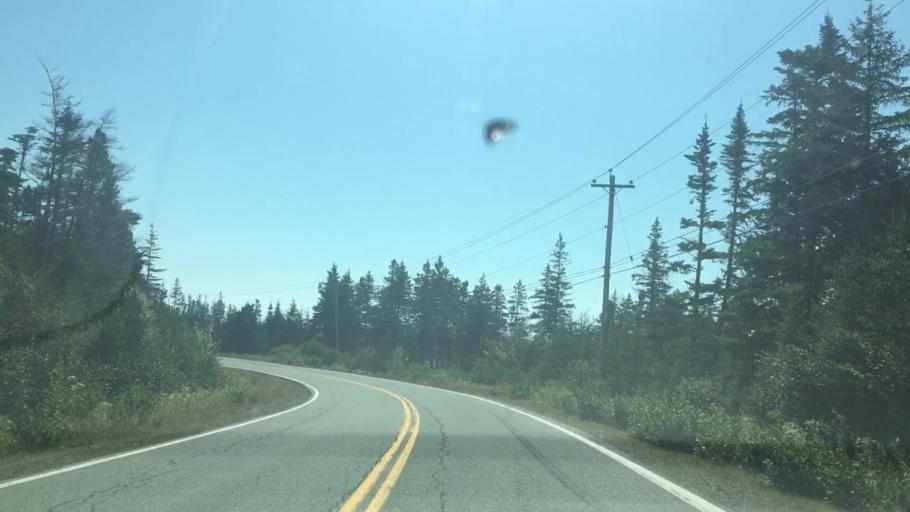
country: CA
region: Nova Scotia
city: Antigonish
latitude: 45.0082
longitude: -62.0901
